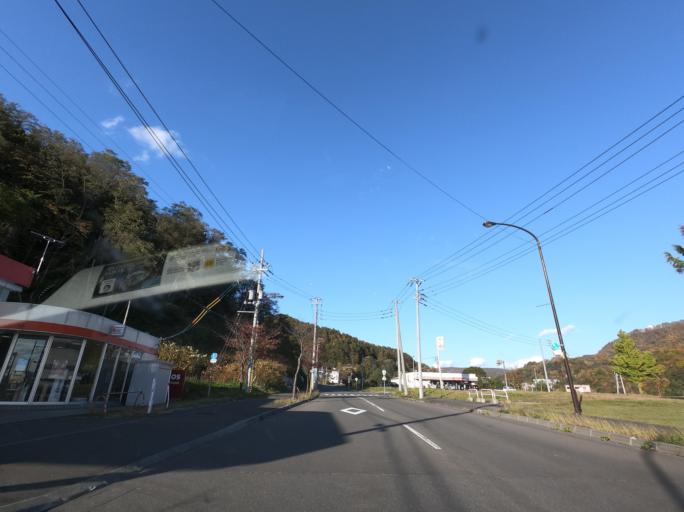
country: JP
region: Hokkaido
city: Iwamizawa
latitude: 43.0517
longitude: 141.9675
